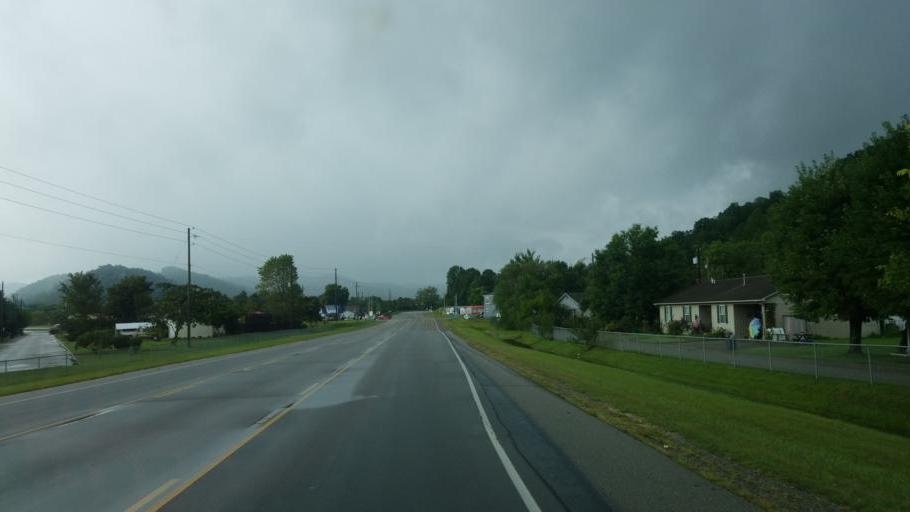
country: US
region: Kentucky
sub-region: Rowan County
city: Morehead
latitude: 38.1721
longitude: -83.4382
